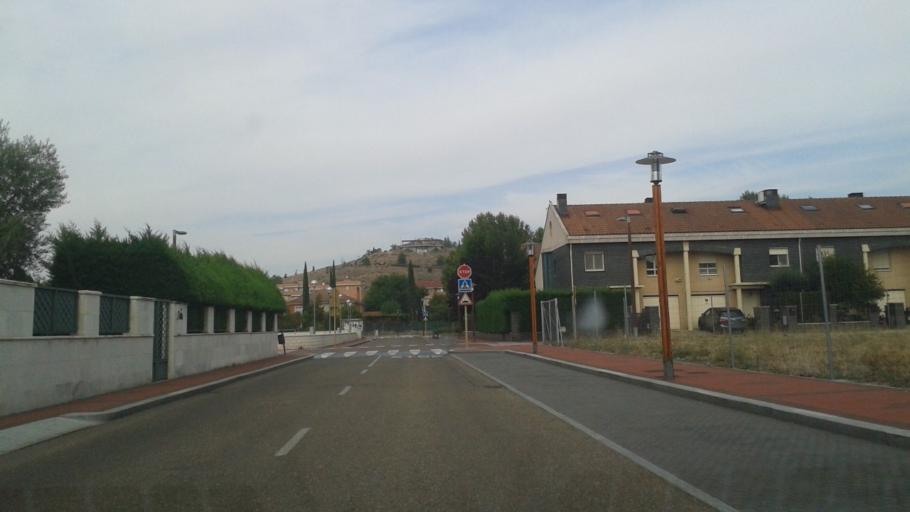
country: ES
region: Castille and Leon
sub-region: Provincia de Valladolid
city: Arroyo
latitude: 41.6127
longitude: -4.7823
